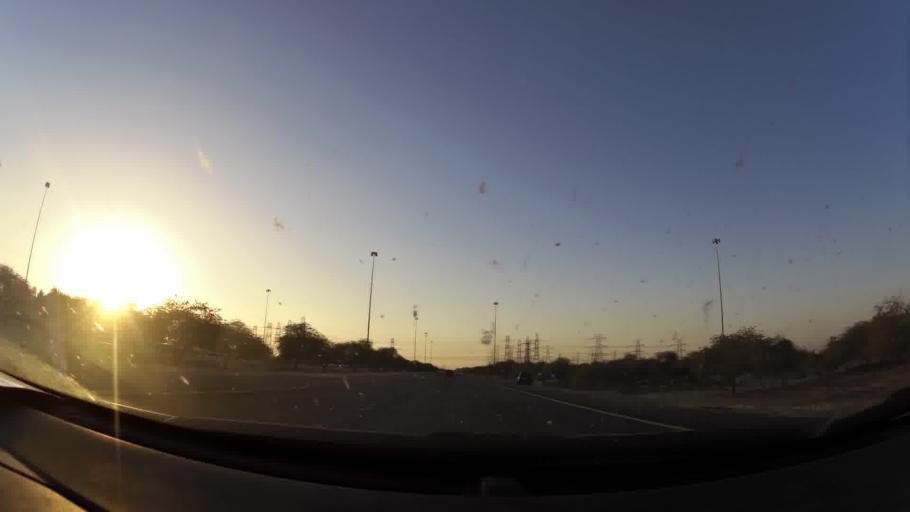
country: KW
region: Al Ahmadi
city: Al Fahahil
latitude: 28.9314
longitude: 48.1803
